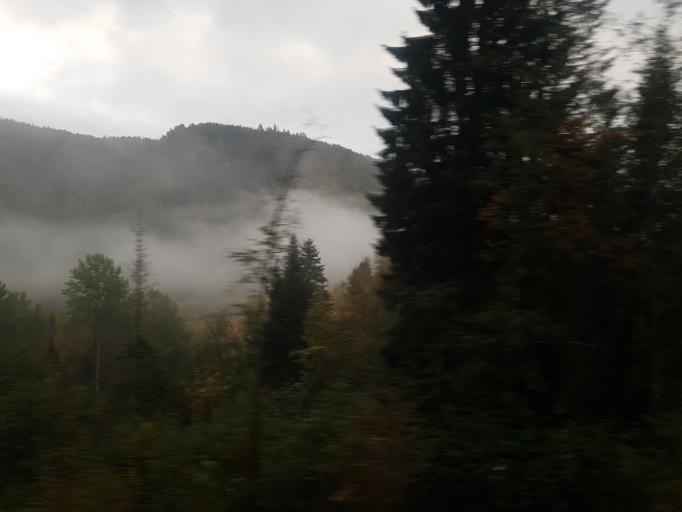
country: NO
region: Sor-Trondelag
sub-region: Midtre Gauldal
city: Storen
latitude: 62.9982
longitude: 10.2417
